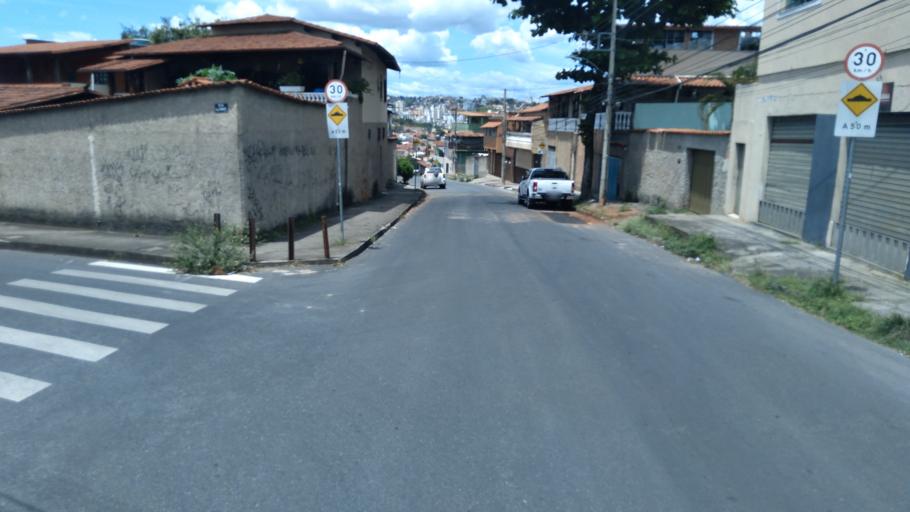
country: BR
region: Minas Gerais
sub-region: Contagem
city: Contagem
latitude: -19.8913
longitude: -44.0134
